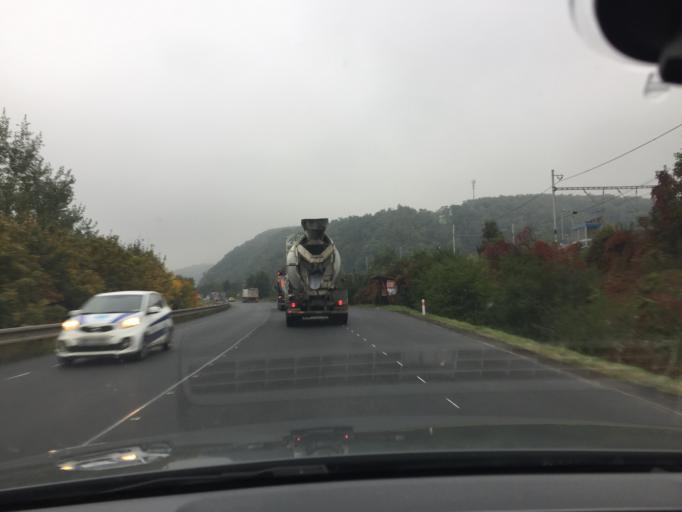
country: CZ
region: Ustecky
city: Lovosice
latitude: 50.5596
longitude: 14.0337
